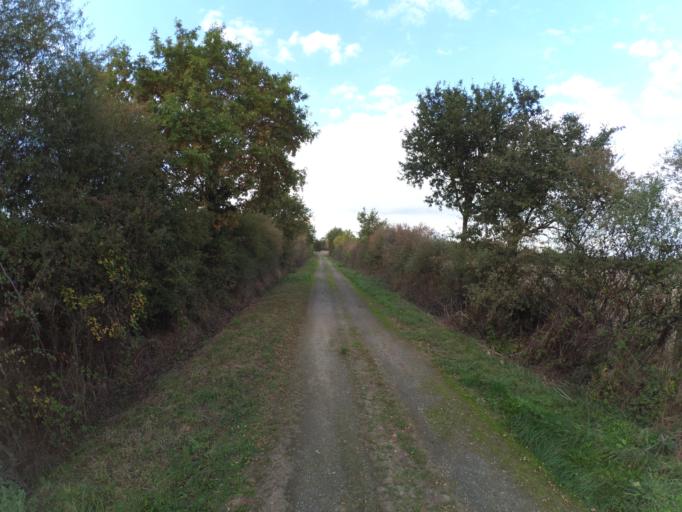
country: FR
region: Pays de la Loire
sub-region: Departement de la Loire-Atlantique
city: Saint-Lumine-de-Clisson
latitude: 47.0773
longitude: -1.3352
